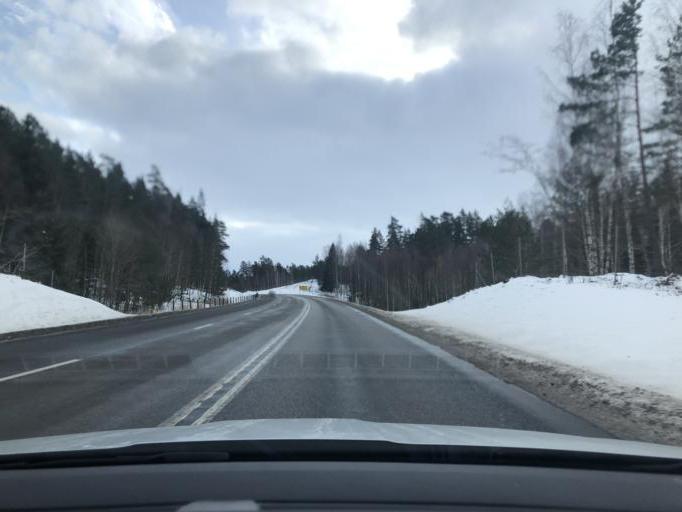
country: SE
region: OEstergoetland
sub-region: Motala Kommun
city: Borensberg
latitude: 58.5662
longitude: 15.3037
